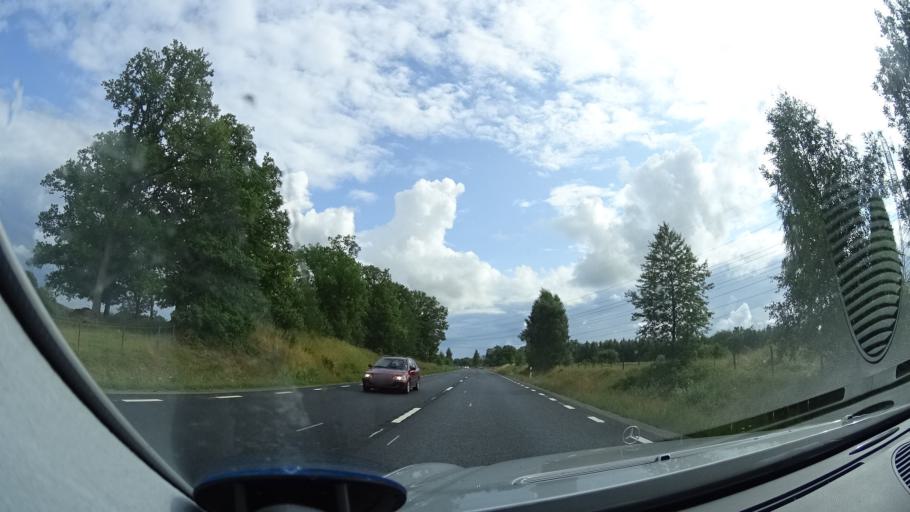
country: SE
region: Blekinge
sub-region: Karlshamns Kommun
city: Karlshamn
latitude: 56.2130
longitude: 14.8118
